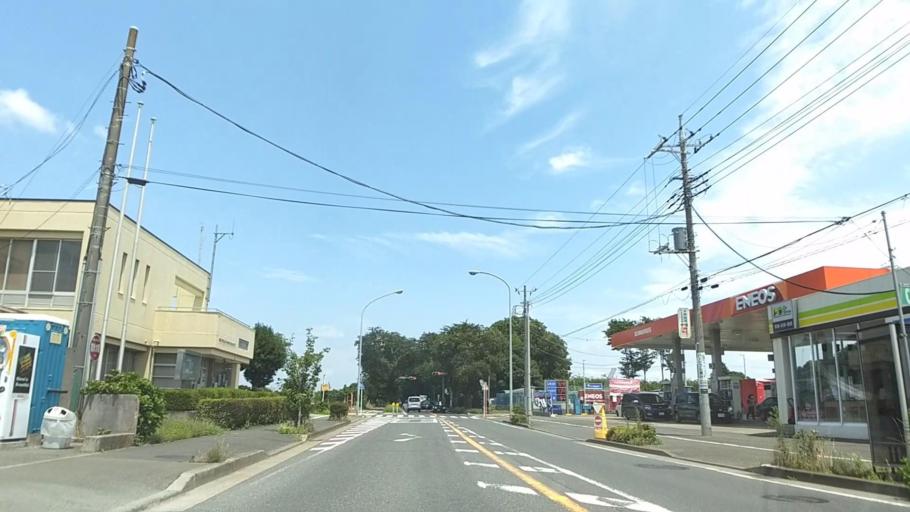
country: JP
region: Kanagawa
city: Minami-rinkan
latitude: 35.4835
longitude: 139.4804
